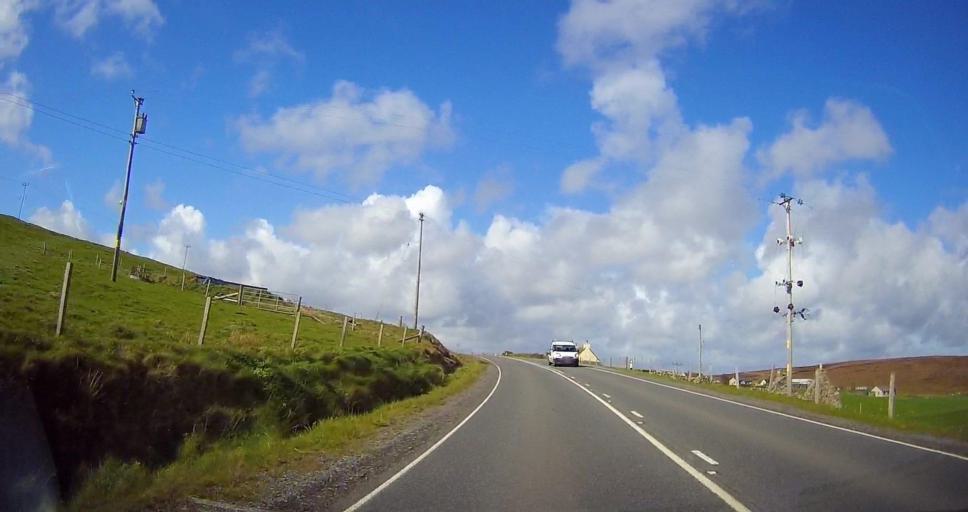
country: GB
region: Scotland
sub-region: Shetland Islands
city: Lerwick
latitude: 60.2369
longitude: -1.2311
